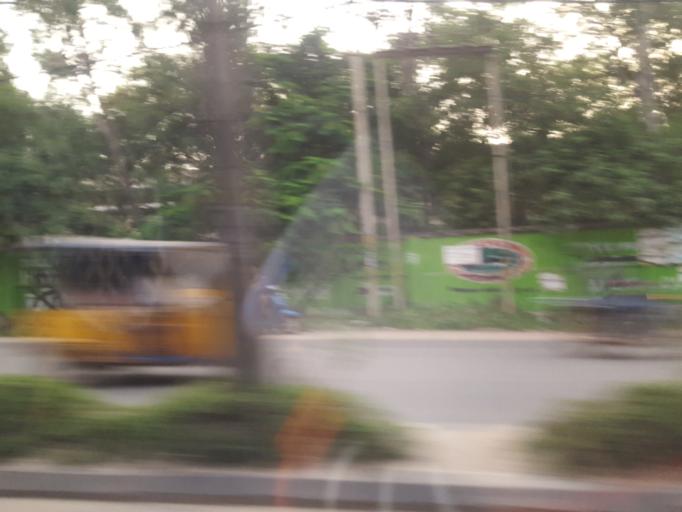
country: IN
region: Telangana
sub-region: Rangareddi
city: Kukatpalli
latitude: 17.5119
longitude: 78.3614
